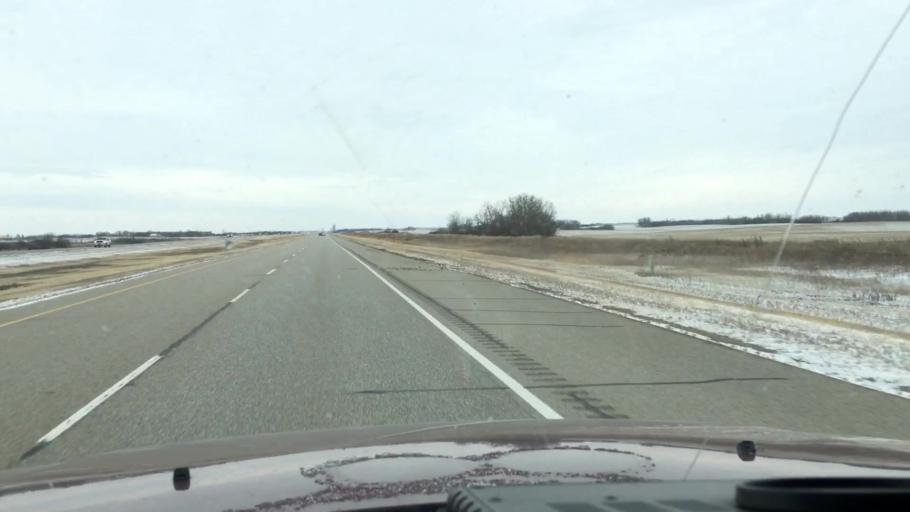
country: CA
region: Saskatchewan
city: Watrous
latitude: 51.3250
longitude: -106.0733
